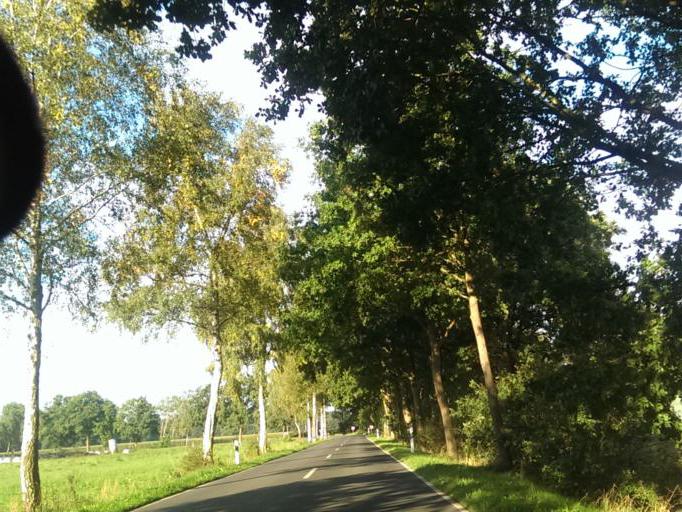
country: DE
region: Lower Saxony
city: Garbsen-Mitte
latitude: 52.4853
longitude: 9.6323
